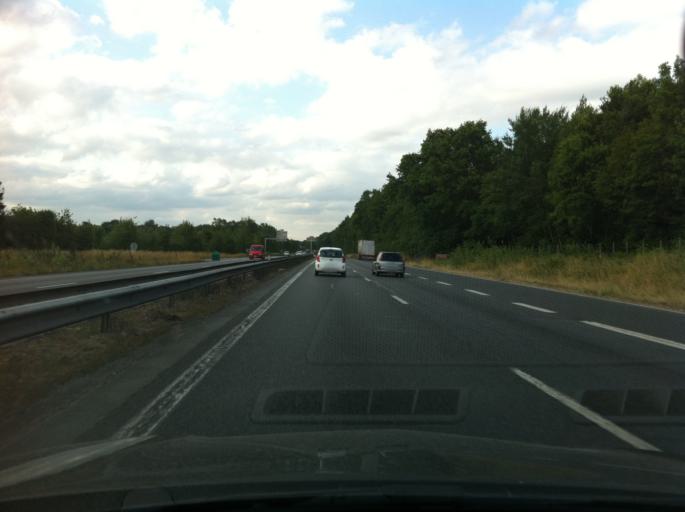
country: FR
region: Ile-de-France
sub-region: Departement de Seine-et-Marne
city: Lesigny
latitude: 48.7507
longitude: 2.6142
